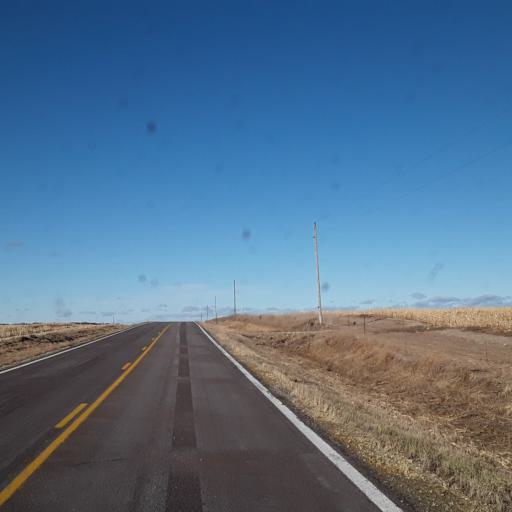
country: US
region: Kansas
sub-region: Cloud County
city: Concordia
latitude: 39.5283
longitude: -97.7228
